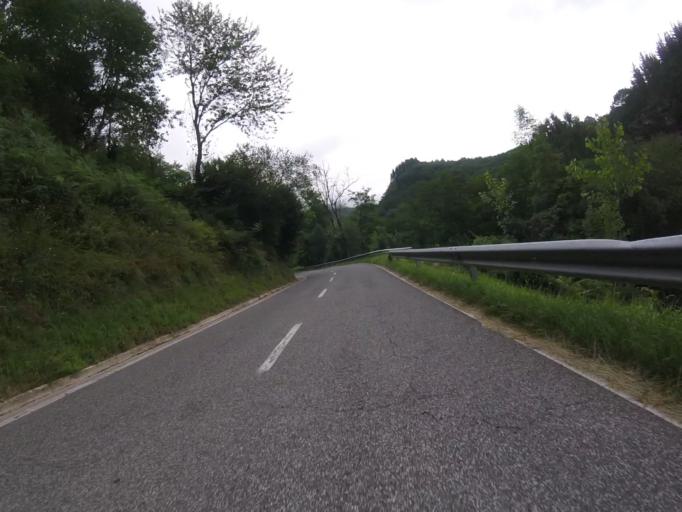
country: ES
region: Navarre
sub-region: Provincia de Navarra
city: Zubieta
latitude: 43.1212
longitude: -1.7540
